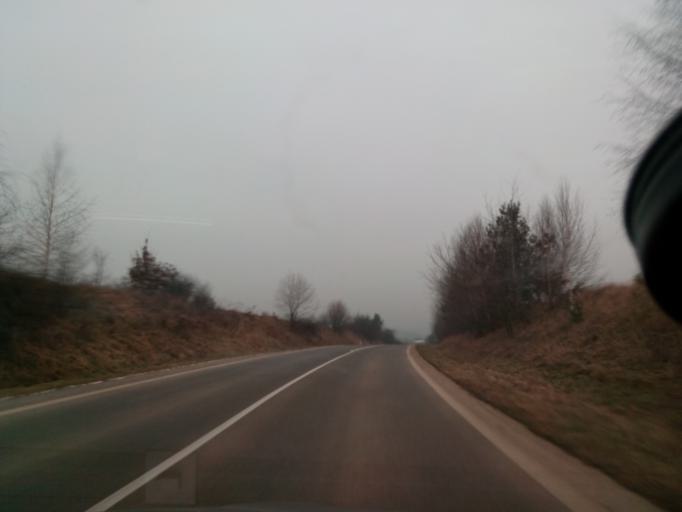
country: SK
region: Kosicky
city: Moldava nad Bodvou
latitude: 48.6751
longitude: 21.1081
